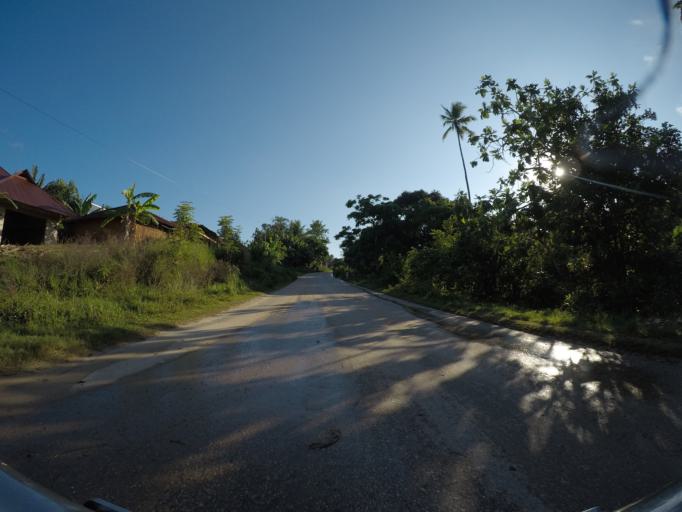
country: TZ
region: Pemba South
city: Mtambile
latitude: -5.3703
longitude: 39.7078
